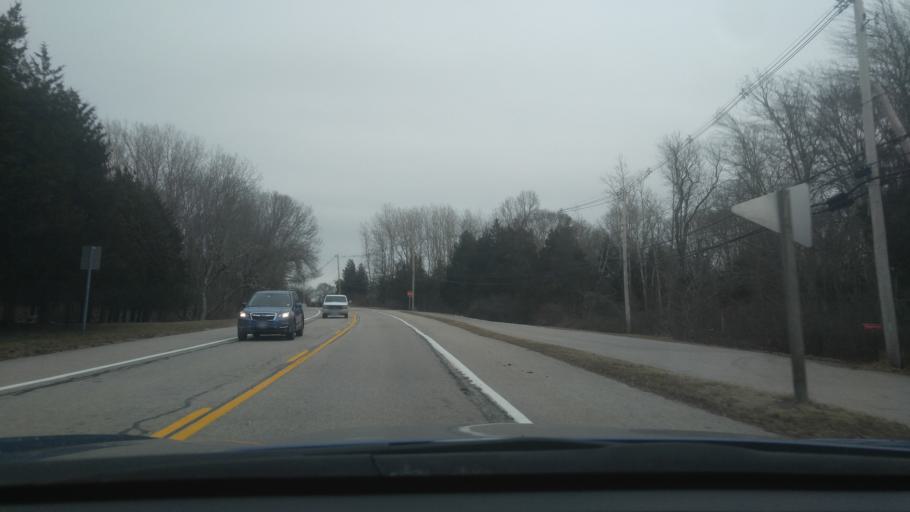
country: US
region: Rhode Island
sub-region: Washington County
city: North Kingstown
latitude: 41.5417
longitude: -71.4405
